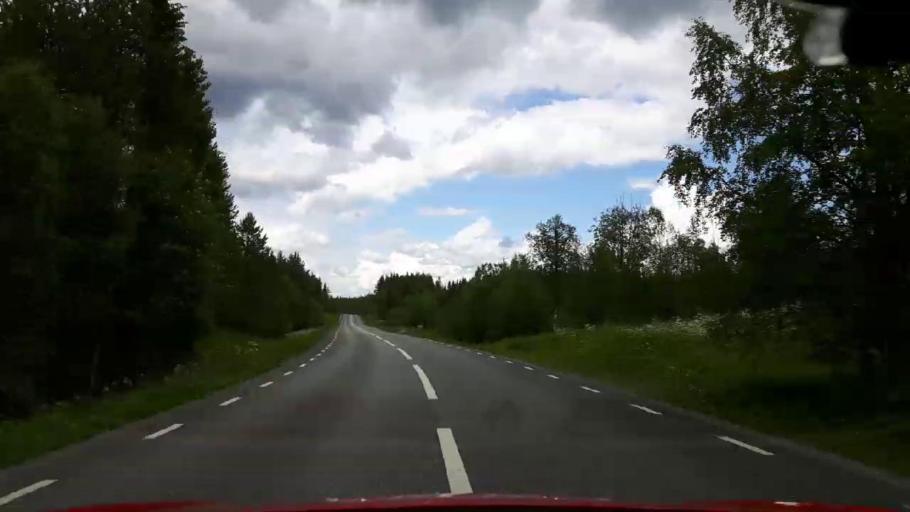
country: SE
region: Jaemtland
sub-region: Krokoms Kommun
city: Krokom
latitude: 63.7937
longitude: 14.3829
